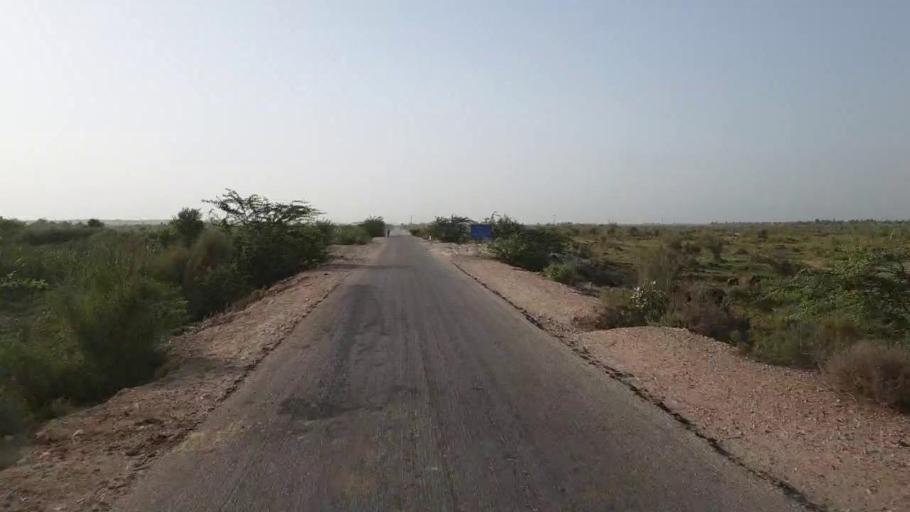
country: PK
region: Sindh
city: Jam Sahib
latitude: 26.4484
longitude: 68.8635
